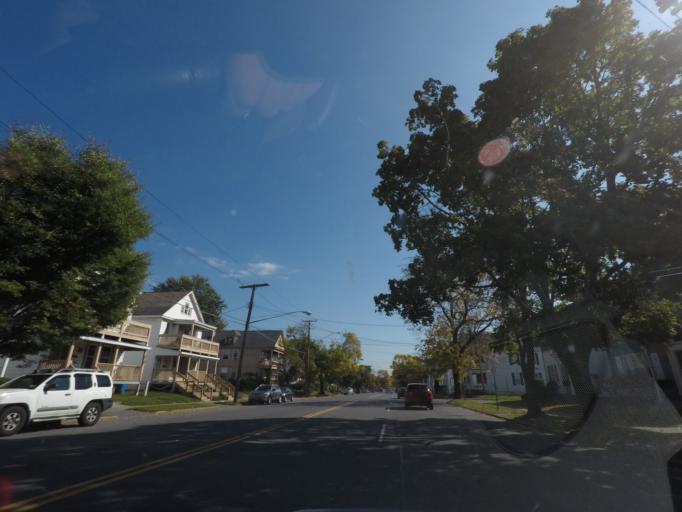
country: US
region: New York
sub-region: Albany County
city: West Albany
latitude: 42.6702
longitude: -73.7865
